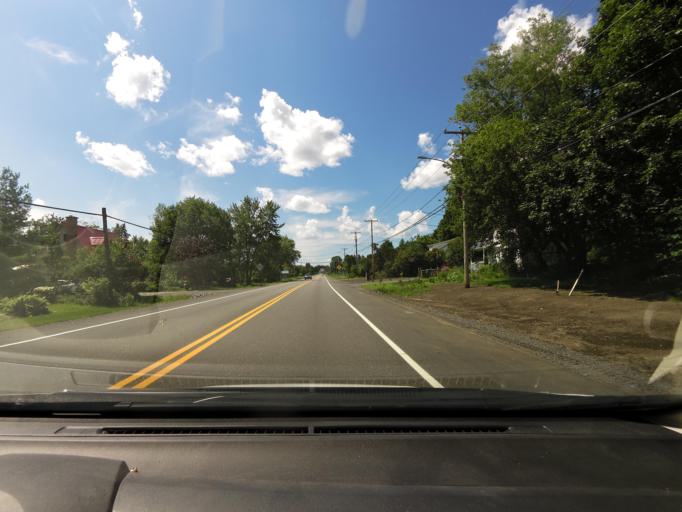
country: CA
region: Quebec
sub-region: Capitale-Nationale
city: Neuville
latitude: 46.7159
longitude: -71.5507
